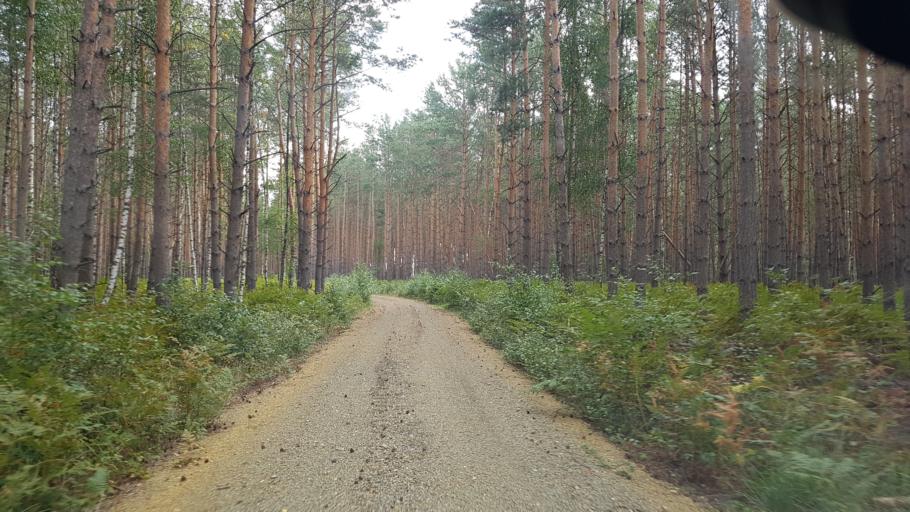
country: DE
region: Brandenburg
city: Ruckersdorf
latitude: 51.5723
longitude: 13.6328
